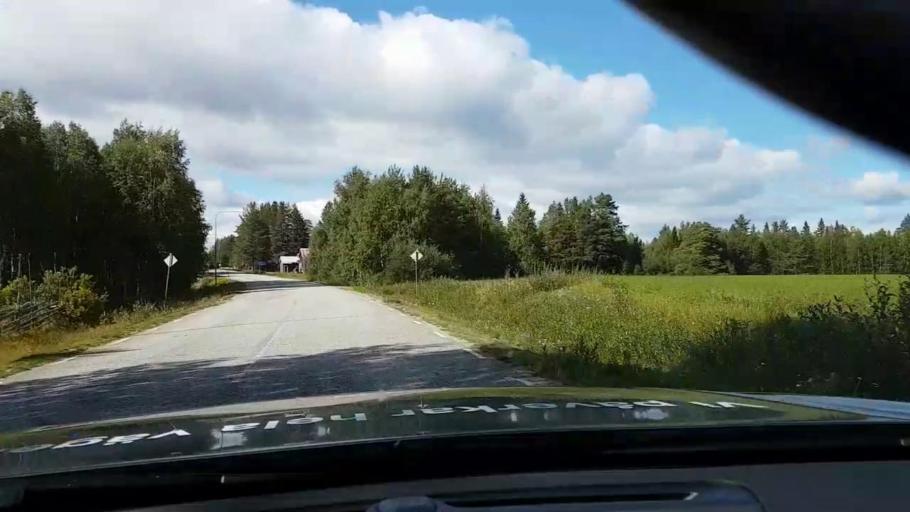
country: SE
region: Vaesterbotten
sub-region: Asele Kommun
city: Asele
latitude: 63.9359
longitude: 17.2877
